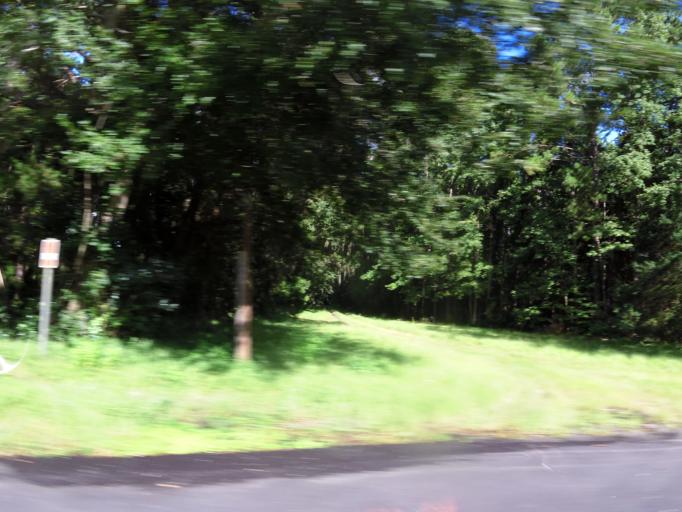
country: US
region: Georgia
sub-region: Camden County
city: Woodbine
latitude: 31.0321
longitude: -81.7304
